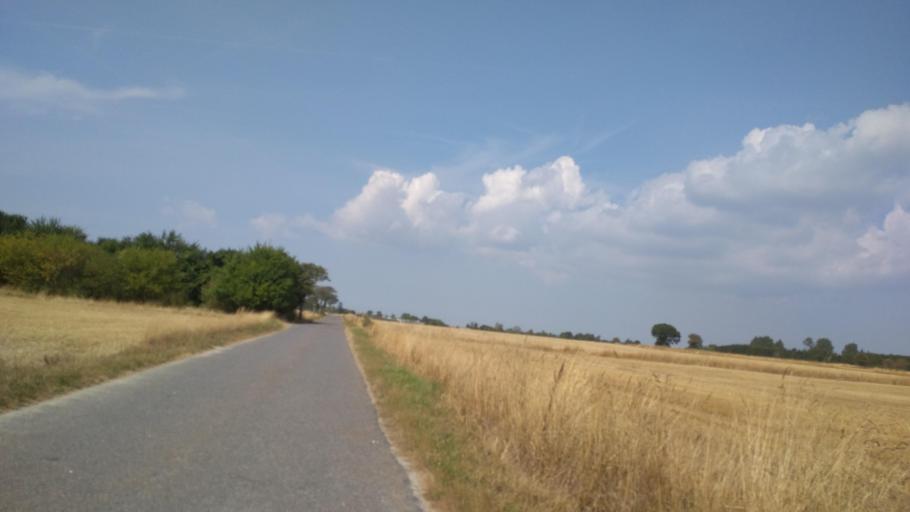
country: DK
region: Capital Region
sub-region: Bornholm Kommune
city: Akirkeby
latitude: 55.0644
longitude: 14.9361
